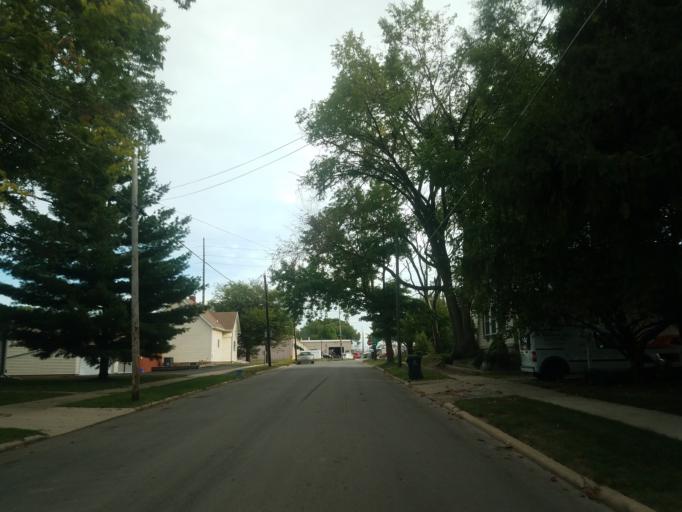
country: US
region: Illinois
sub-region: McLean County
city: Bloomington
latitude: 40.4674
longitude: -88.9855
